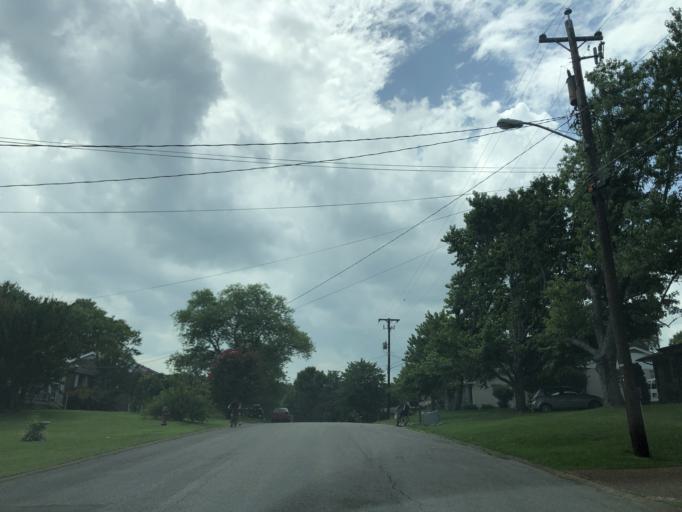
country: US
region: Tennessee
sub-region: Williamson County
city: Brentwood Estates
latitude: 36.0587
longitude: -86.6917
